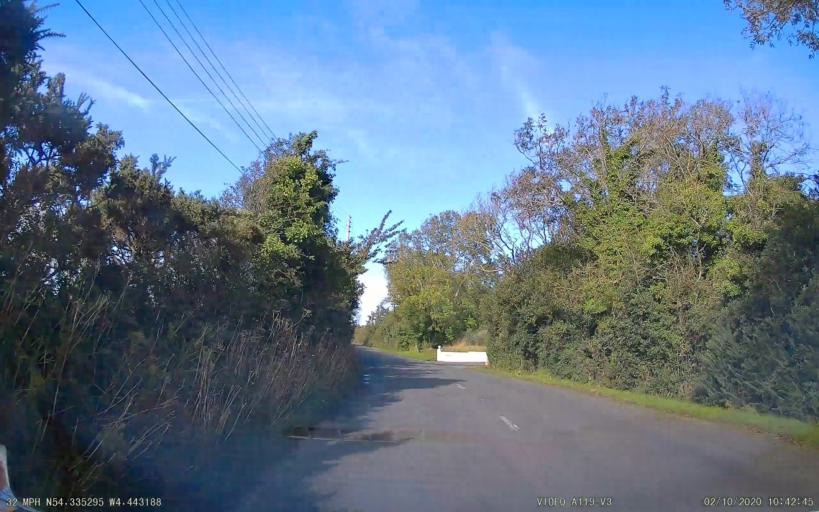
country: IM
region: Ramsey
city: Ramsey
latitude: 54.3353
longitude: -4.4432
